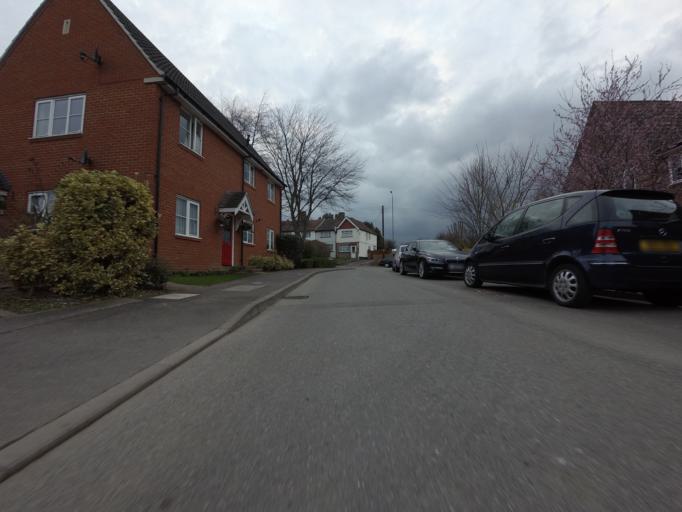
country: GB
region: England
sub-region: Kent
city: Swanley
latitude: 51.4025
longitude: 0.1839
